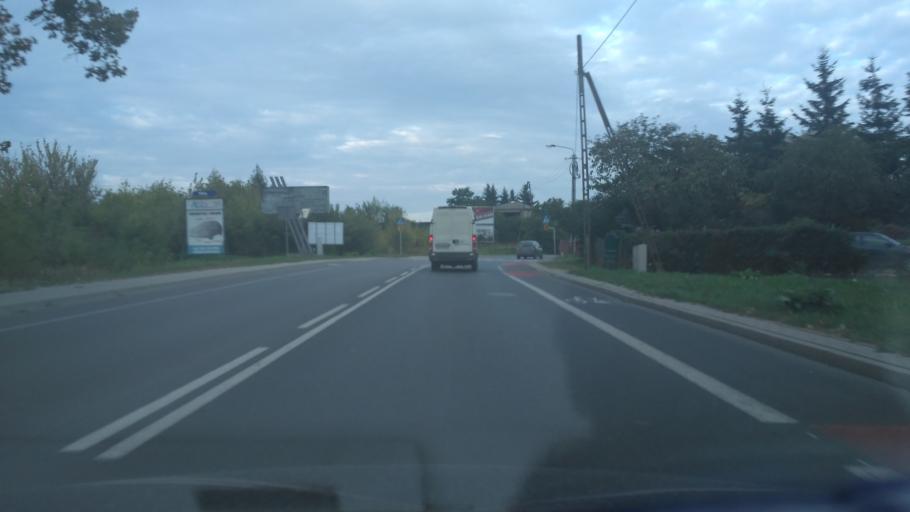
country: PL
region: Lublin Voivodeship
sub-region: Powiat lubelski
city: Jakubowice Murowane
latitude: 51.2590
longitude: 22.6141
